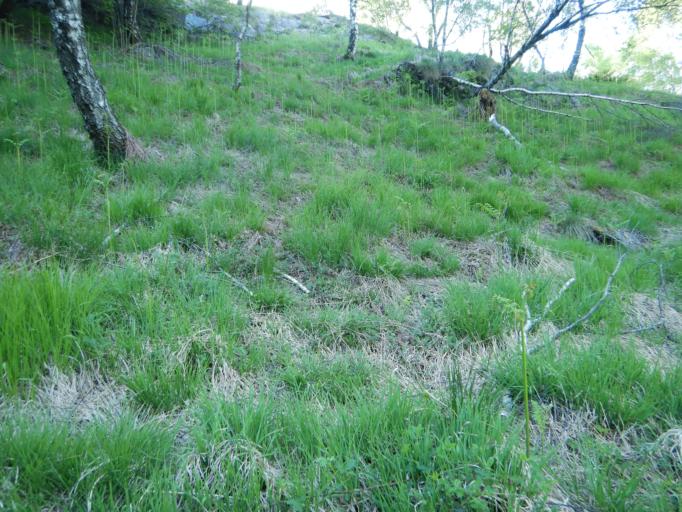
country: CH
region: Ticino
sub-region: Bellinzona District
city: Cadenazzo
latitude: 46.1321
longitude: 8.9566
